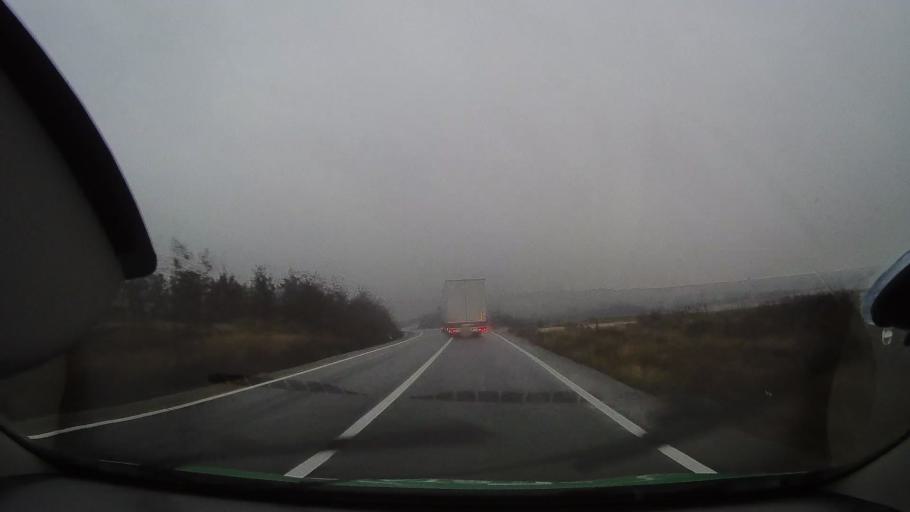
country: RO
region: Bihor
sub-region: Comuna Olcea
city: Calacea
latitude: 46.6504
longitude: 21.9584
